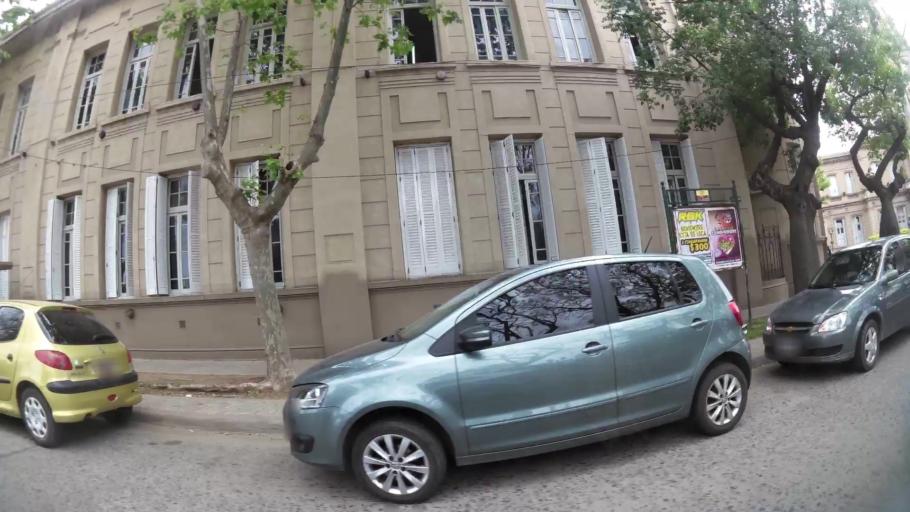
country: AR
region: Buenos Aires
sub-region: Partido de Campana
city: Campana
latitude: -34.1639
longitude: -58.9596
